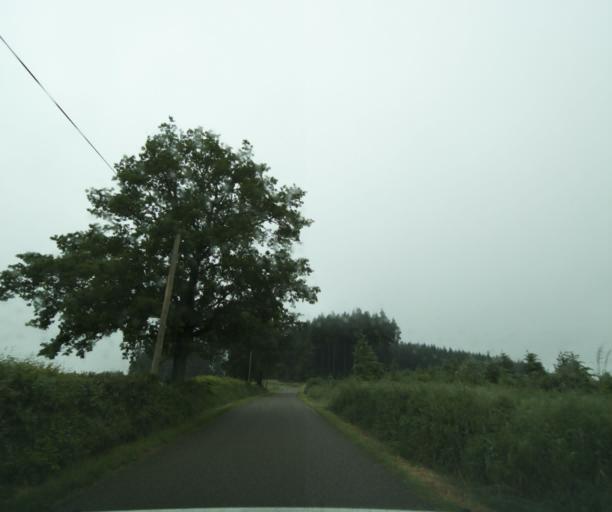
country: FR
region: Bourgogne
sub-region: Departement de Saone-et-Loire
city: Charolles
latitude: 46.4052
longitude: 4.3726
